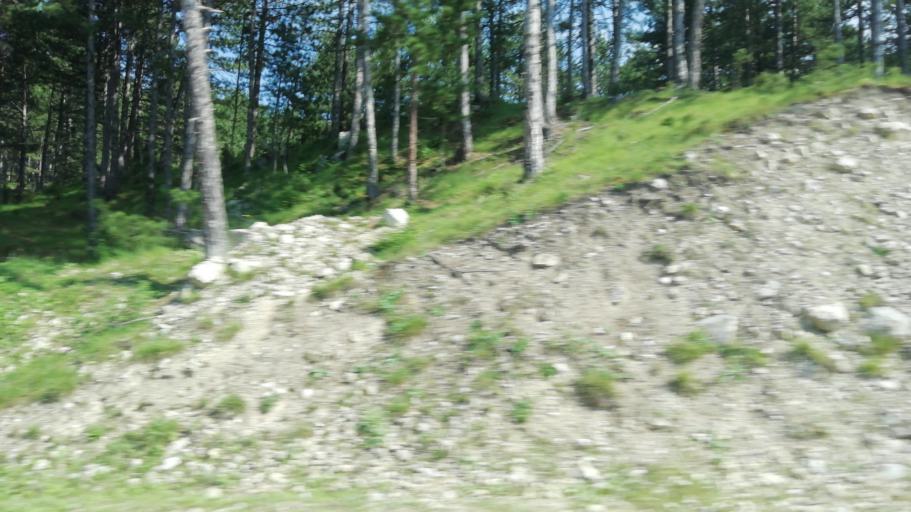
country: TR
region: Karabuk
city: Karabuk
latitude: 41.1204
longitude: 32.5820
